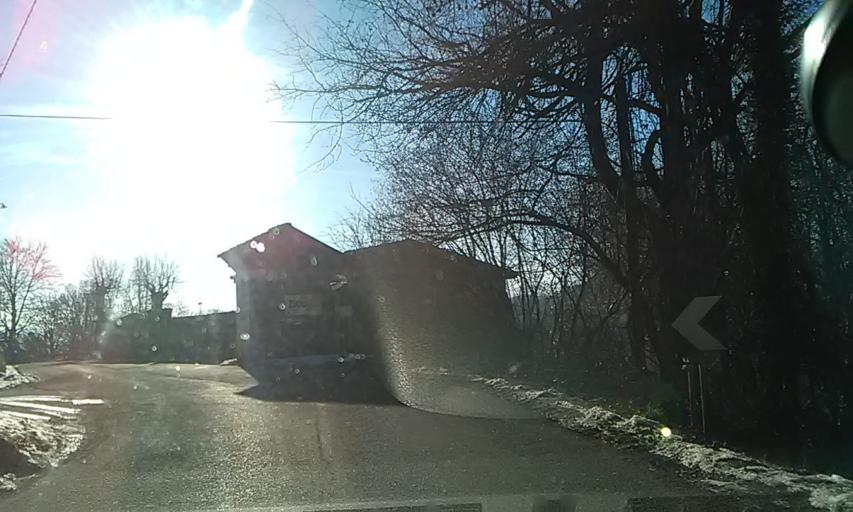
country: IT
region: Piedmont
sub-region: Provincia di Vercelli
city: Valduggia
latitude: 45.7471
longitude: 8.3425
